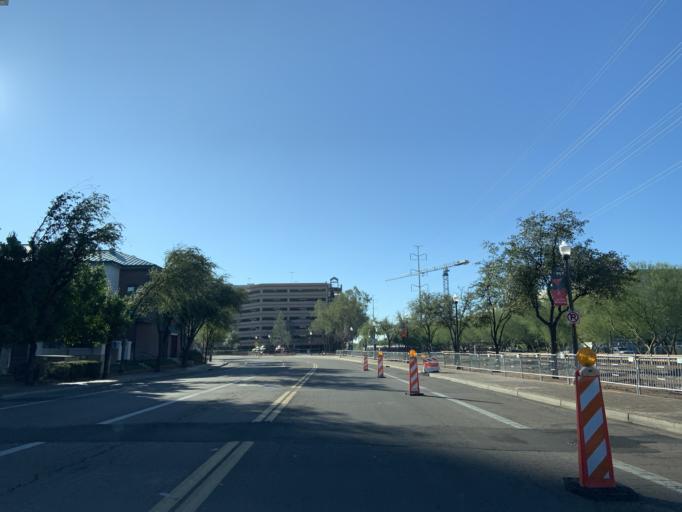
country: US
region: Arizona
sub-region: Maricopa County
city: Tempe Junction
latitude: 33.4252
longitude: -111.9434
